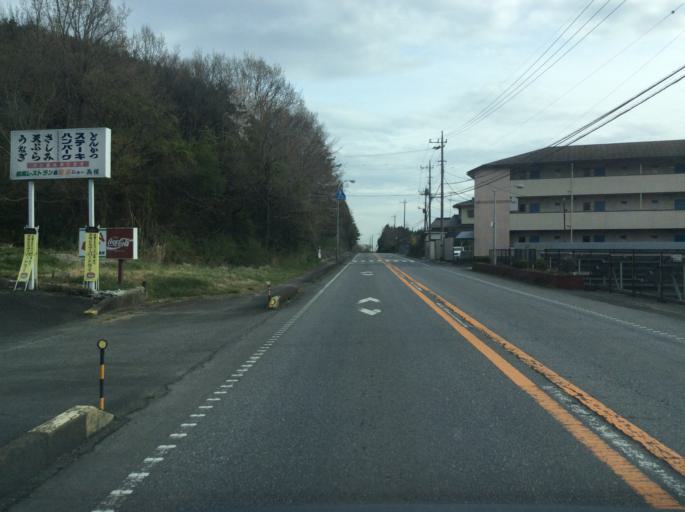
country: JP
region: Ibaraki
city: Tsukuba
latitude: 36.1639
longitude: 140.1069
